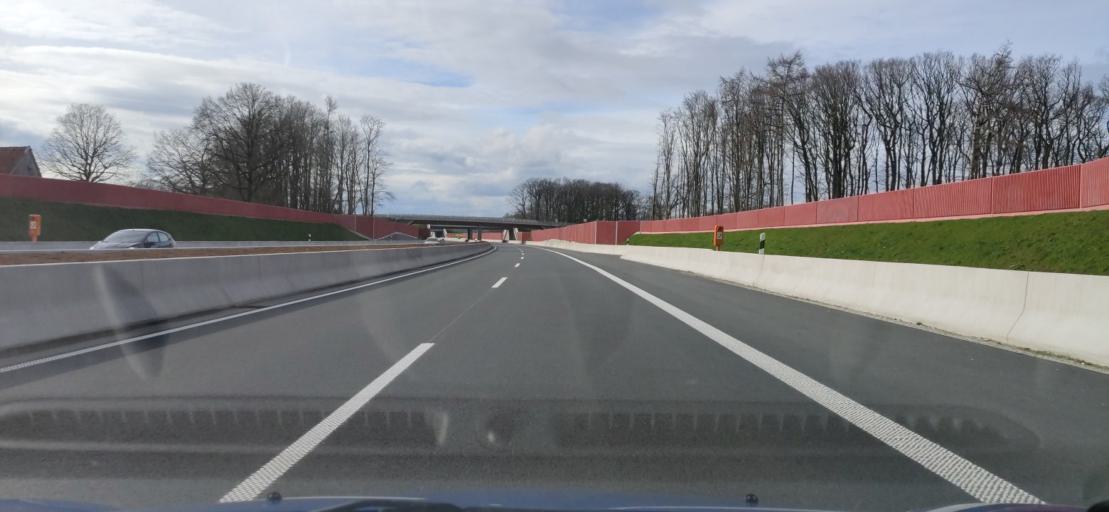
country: DE
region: North Rhine-Westphalia
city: Borgholzhausen
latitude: 52.0688
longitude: 8.2959
